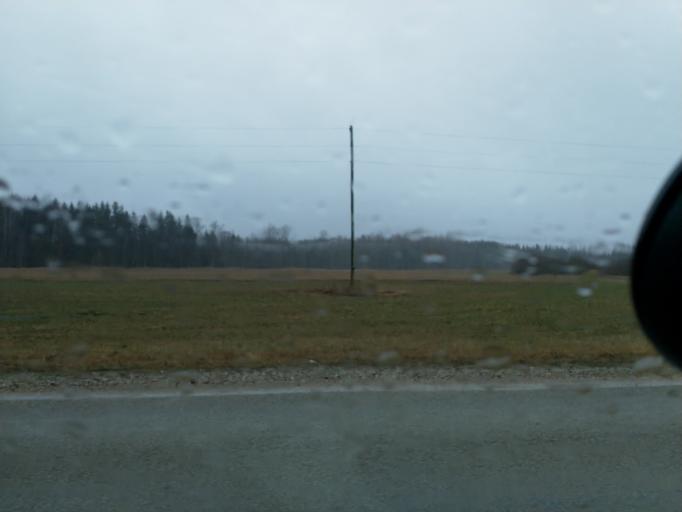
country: LV
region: Saldus Rajons
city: Saldus
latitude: 56.7958
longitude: 22.3132
